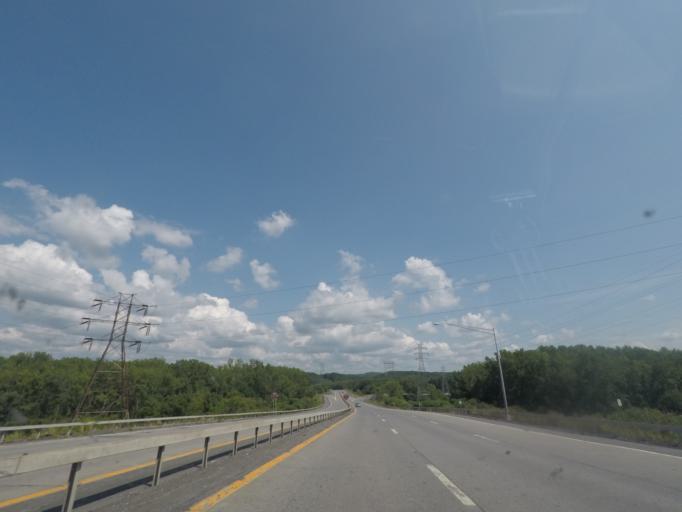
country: US
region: New York
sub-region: Albany County
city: Menands
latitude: 42.6846
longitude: -73.7278
